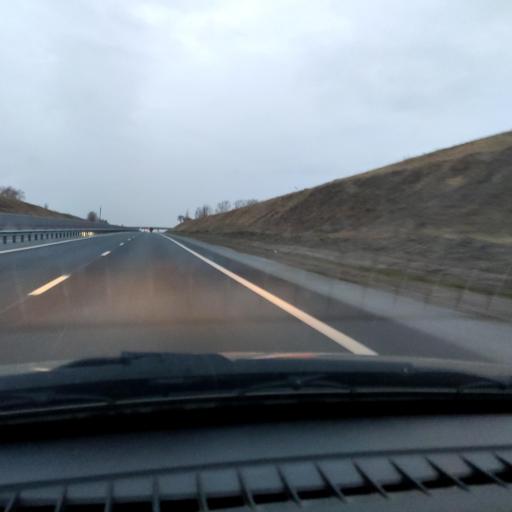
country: RU
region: Samara
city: Mirnyy
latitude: 53.4474
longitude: 50.2576
